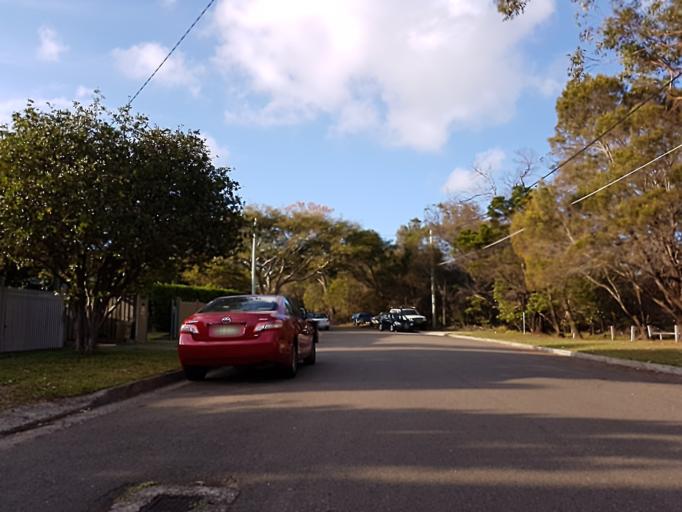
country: AU
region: New South Wales
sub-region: Warringah
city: Allambie Heights
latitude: -33.7800
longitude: 151.2393
